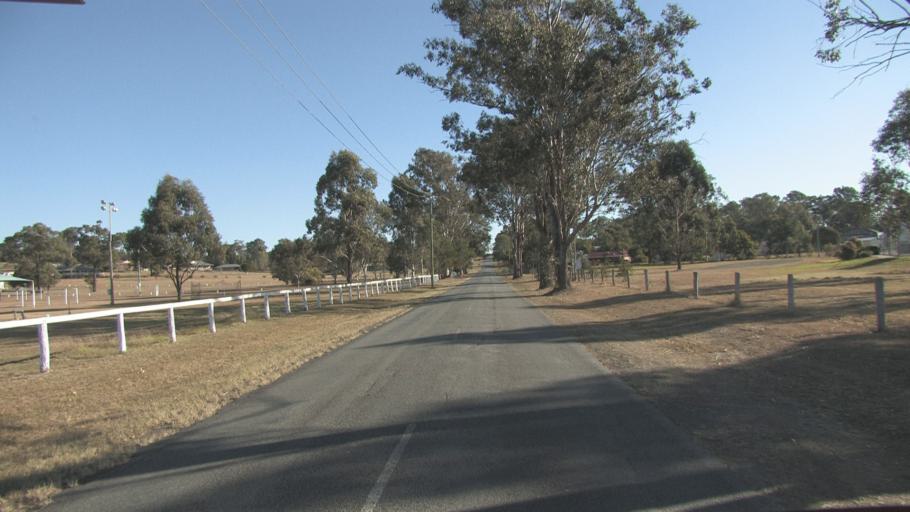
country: AU
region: Queensland
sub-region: Logan
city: Cedar Vale
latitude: -27.8299
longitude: 153.0106
